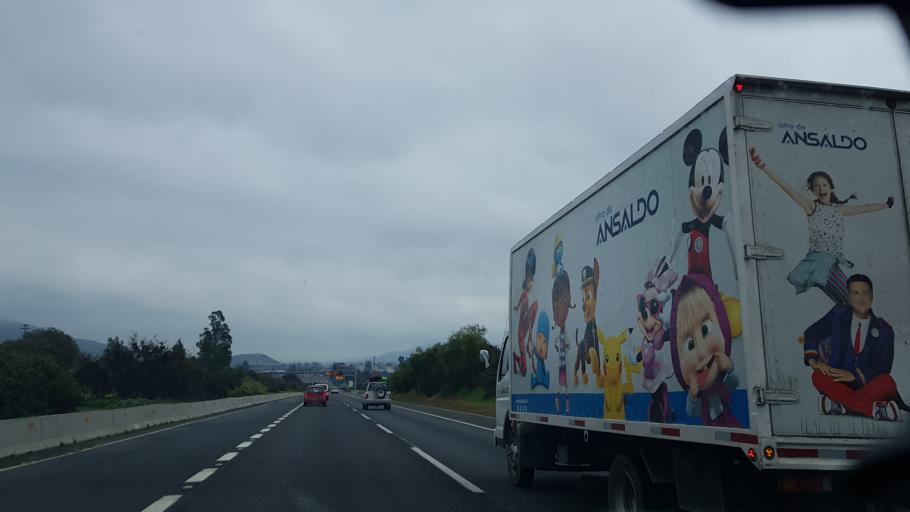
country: CL
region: Santiago Metropolitan
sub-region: Provincia de Melipilla
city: Melipilla
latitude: -33.3756
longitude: -71.2885
